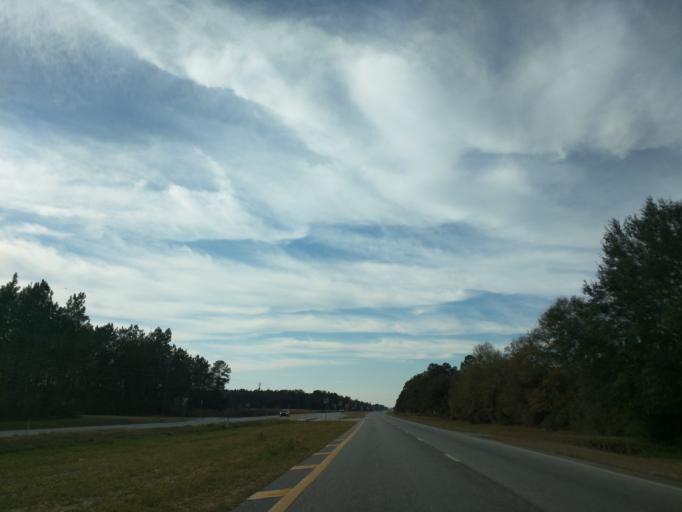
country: US
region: Georgia
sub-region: Decatur County
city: Bainbridge
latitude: 30.8886
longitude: -84.4814
